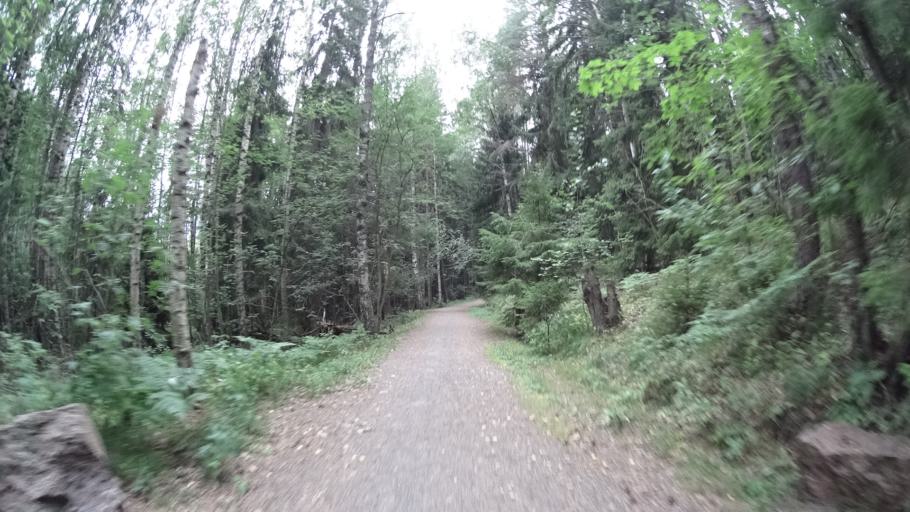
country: FI
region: Uusimaa
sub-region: Helsinki
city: Espoo
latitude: 60.1323
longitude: 24.6743
